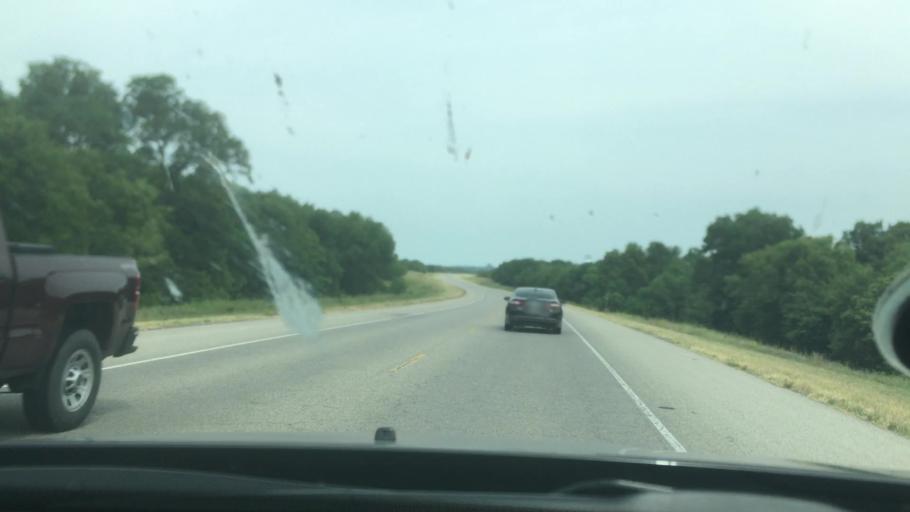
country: US
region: Oklahoma
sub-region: Pontotoc County
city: Ada
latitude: 34.7014
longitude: -96.6030
